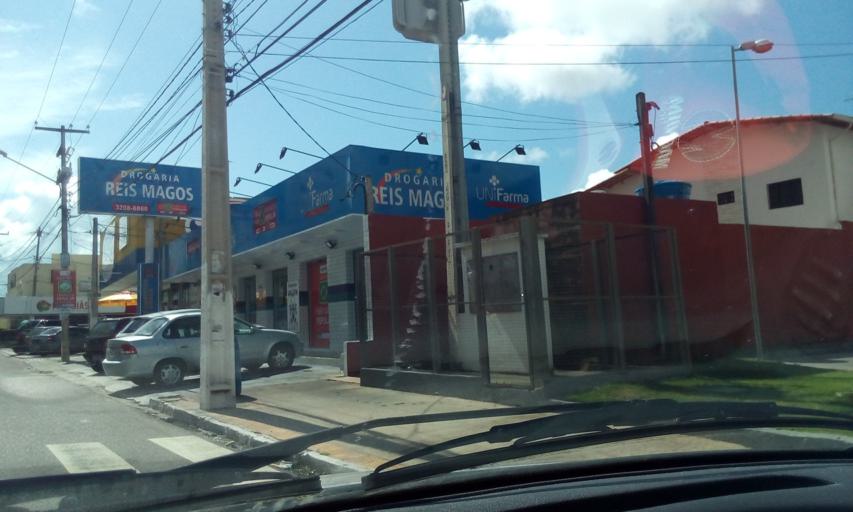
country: BR
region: Rio Grande do Norte
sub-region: Parnamirim
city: Parnamirim
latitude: -5.8782
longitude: -35.2097
